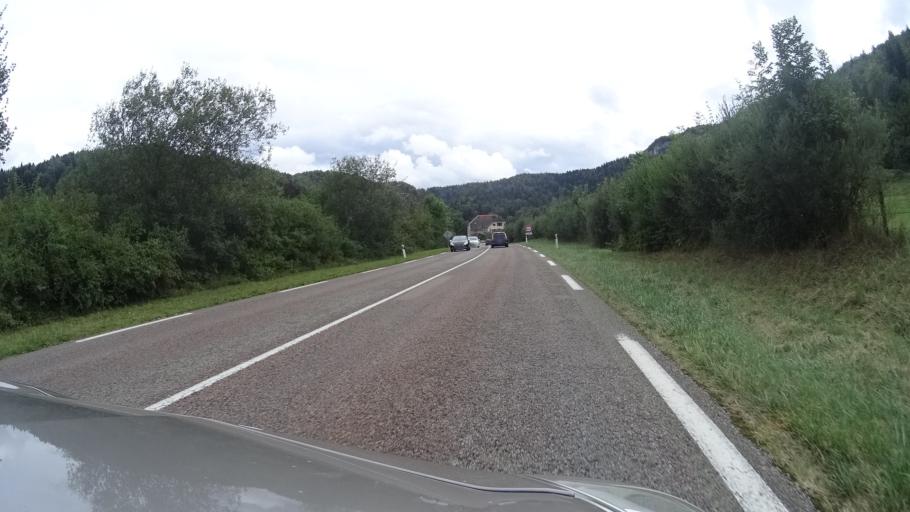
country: FR
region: Franche-Comte
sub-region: Departement du Jura
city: Champagnole
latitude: 46.6789
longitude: 5.9323
